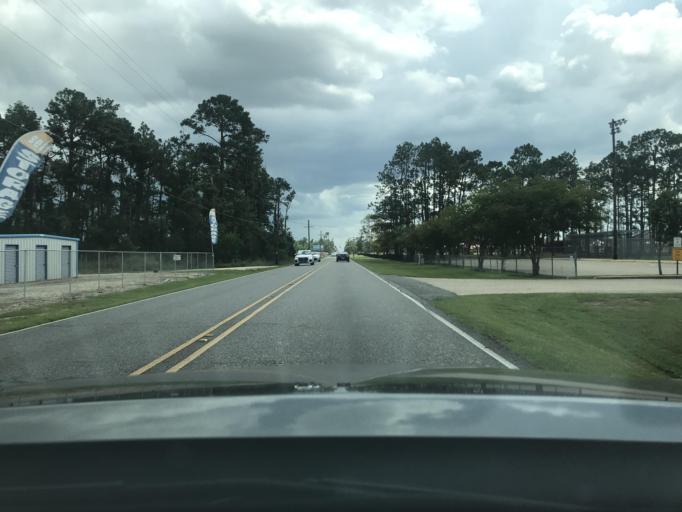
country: US
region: Louisiana
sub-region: Calcasieu Parish
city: Westlake
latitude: 30.2791
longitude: -93.2582
